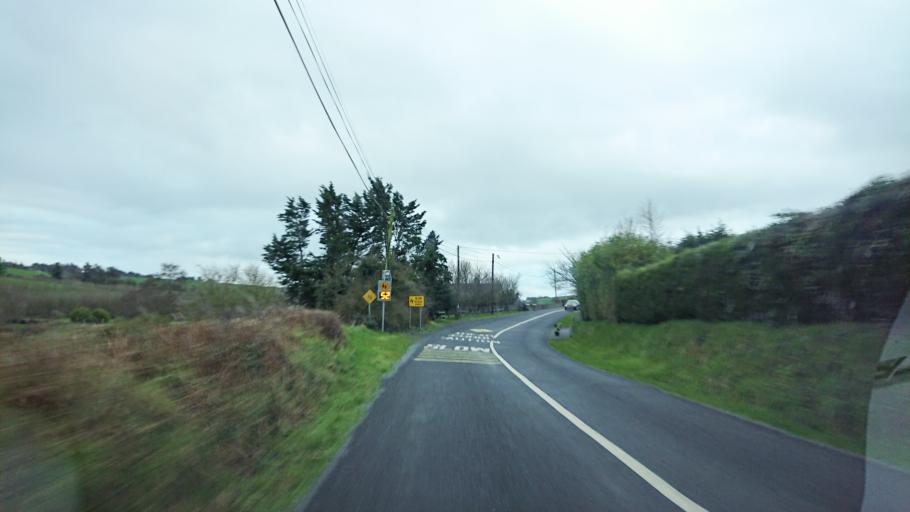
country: IE
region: Munster
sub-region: Waterford
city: Portlaw
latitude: 52.1562
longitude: -7.3836
